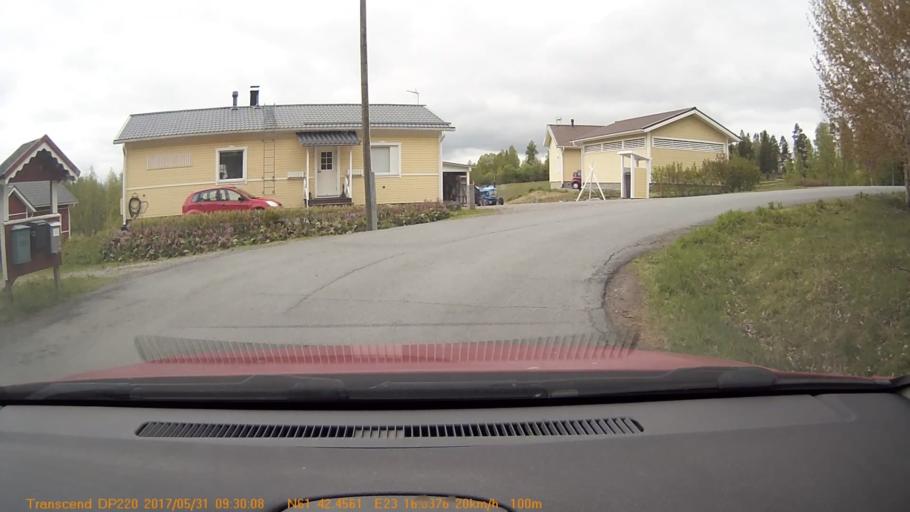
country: FI
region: Pirkanmaa
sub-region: Tampere
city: Viljakkala
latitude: 61.7077
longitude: 23.2808
